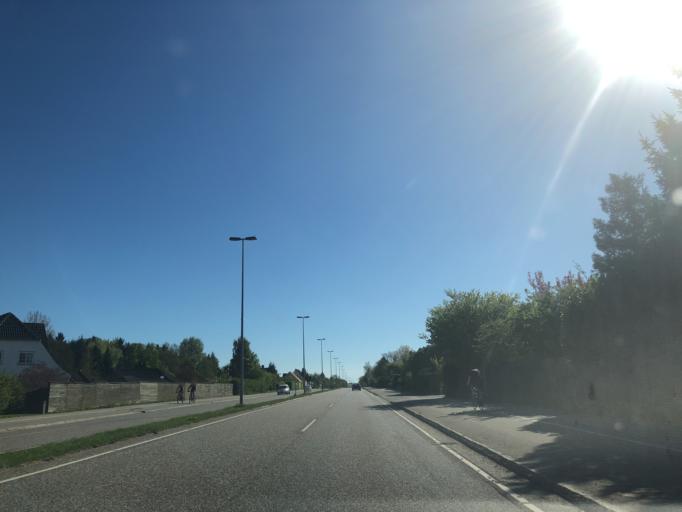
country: DK
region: Zealand
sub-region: Koge Kommune
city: Koge
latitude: 55.4392
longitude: 12.1647
